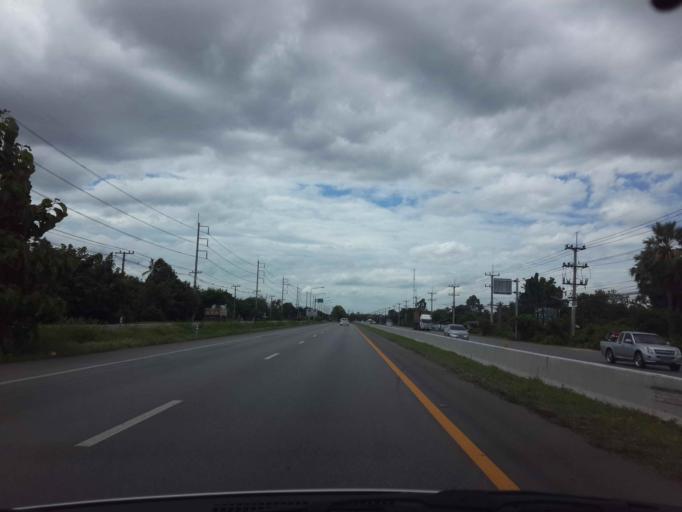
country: TH
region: Phetchaburi
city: Khao Yoi
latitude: 13.1573
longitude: 99.8476
